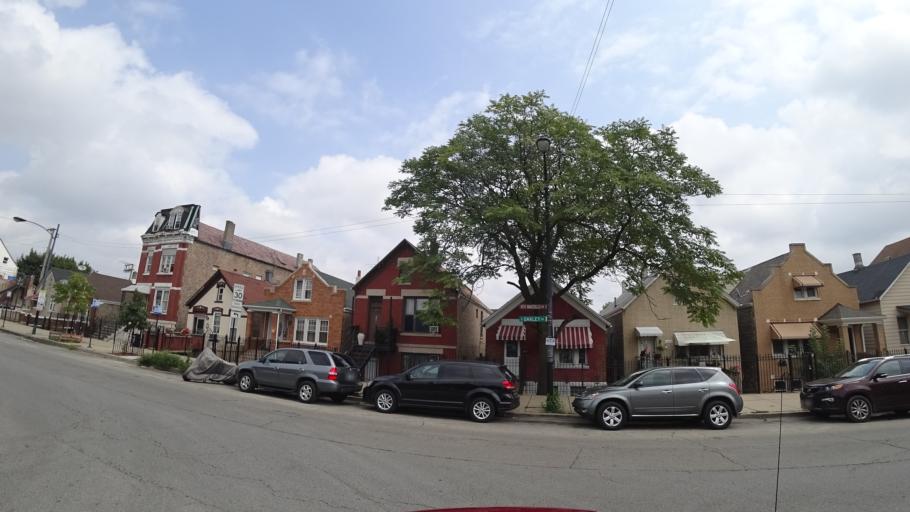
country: US
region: Illinois
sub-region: Cook County
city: Chicago
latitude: 41.8511
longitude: -87.6833
